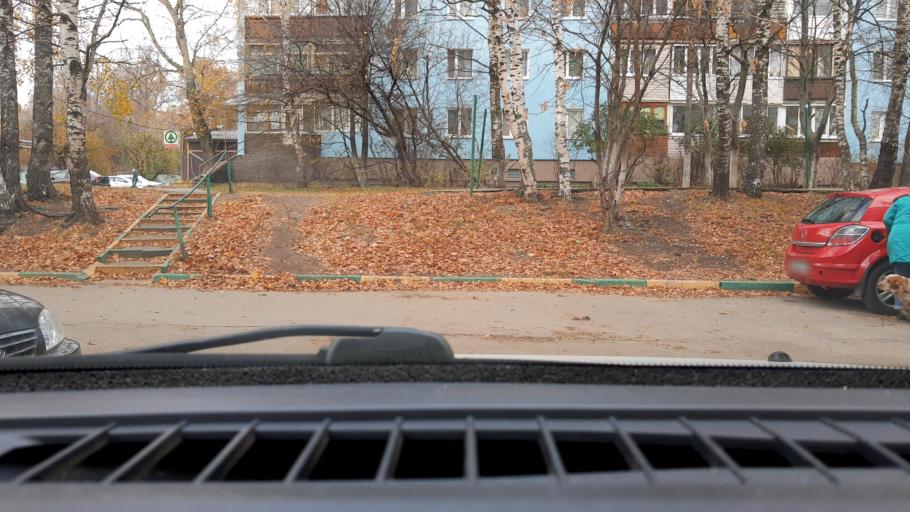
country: RU
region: Nizjnij Novgorod
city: Nizhniy Novgorod
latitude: 56.2616
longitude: 43.9973
